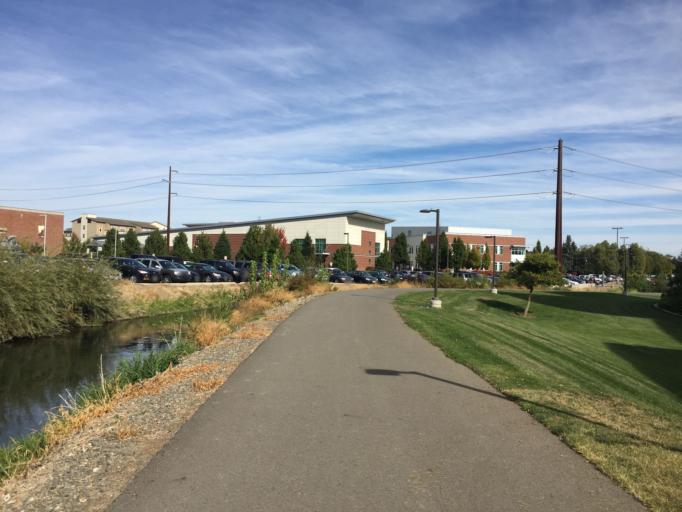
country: US
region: Washington
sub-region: Kittitas County
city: Ellensburg
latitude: 47.0048
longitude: -120.5364
